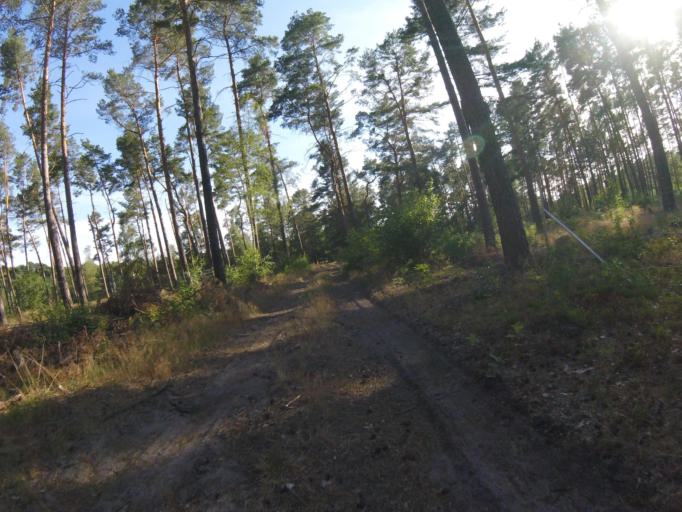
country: DE
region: Berlin
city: Schmockwitz
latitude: 52.3258
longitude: 13.7240
